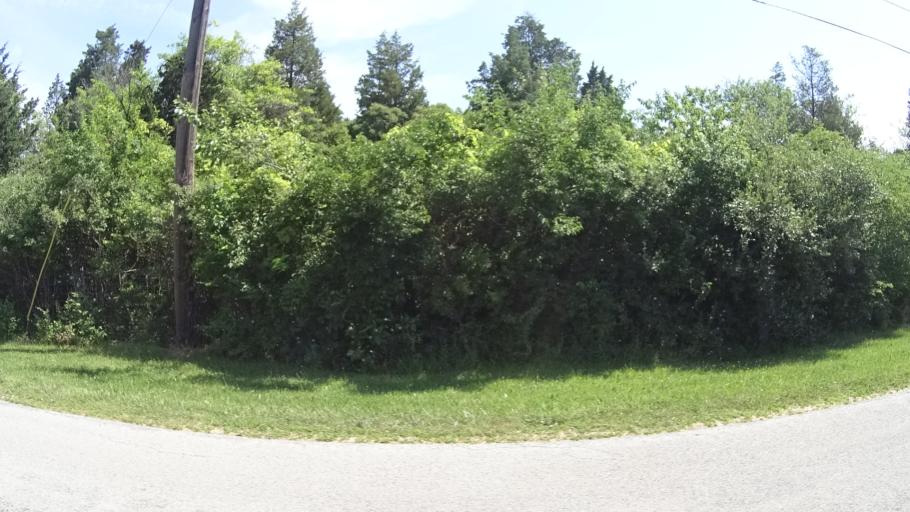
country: US
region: Ohio
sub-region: Erie County
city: Sandusky
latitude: 41.4305
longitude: -82.7735
